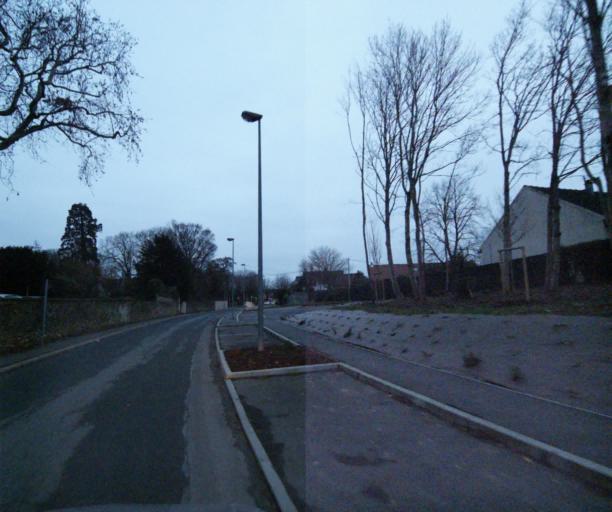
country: FR
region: Ile-de-France
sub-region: Departement de Seine-et-Marne
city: Dammartin-en-Goele
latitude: 49.0559
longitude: 2.6737
